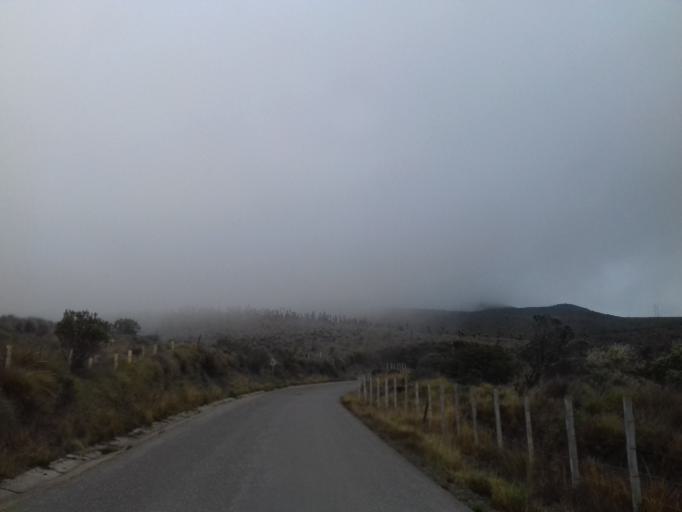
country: CO
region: Caldas
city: Villamaria
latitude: 4.9800
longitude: -75.3353
